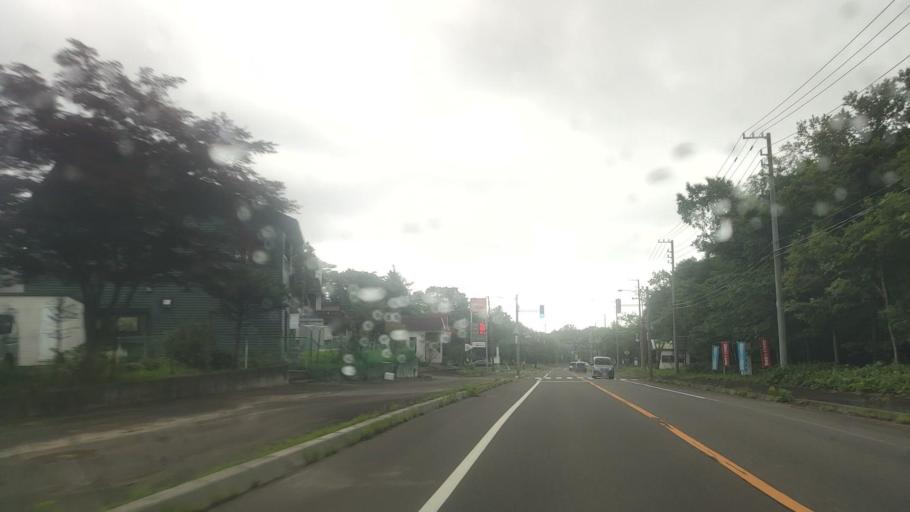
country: JP
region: Hokkaido
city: Shiraoi
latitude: 42.4767
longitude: 141.1469
